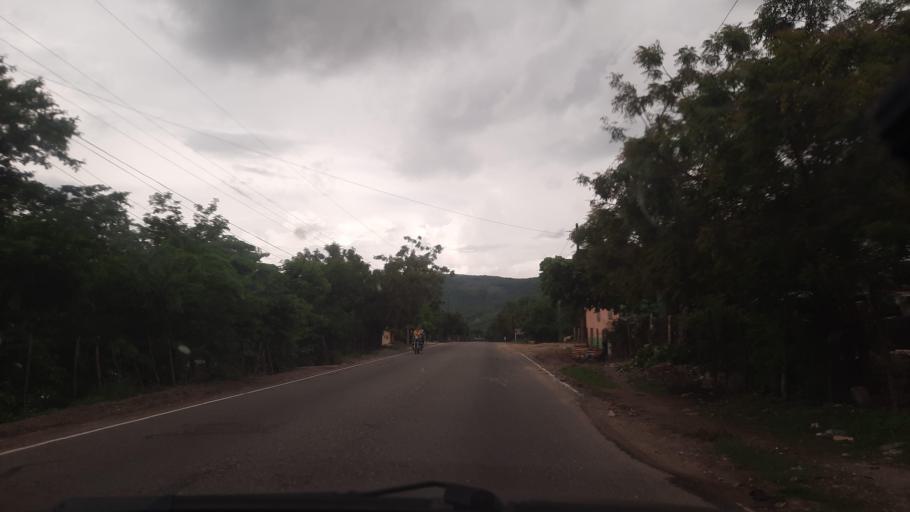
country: GT
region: Zacapa
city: Zacapa
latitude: 14.9181
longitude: -89.5297
